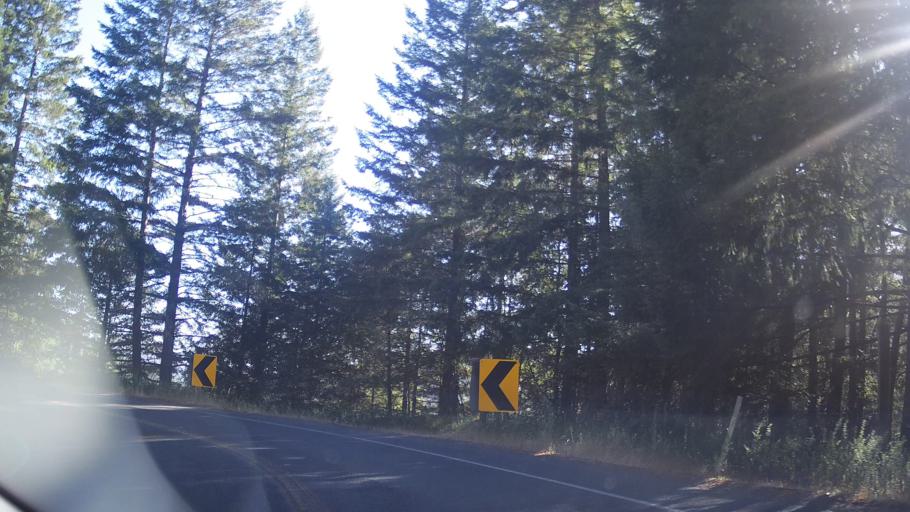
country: US
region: California
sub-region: Mendocino County
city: Brooktrails
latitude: 39.3720
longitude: -123.4970
